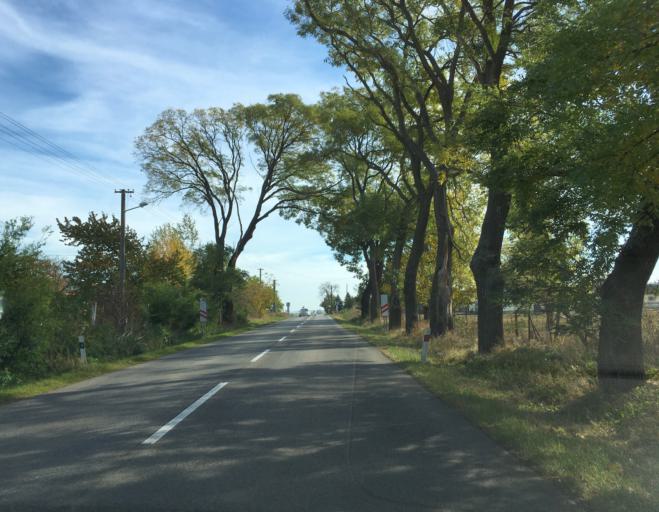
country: SK
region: Nitriansky
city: Zeliezovce
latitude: 48.0974
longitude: 18.5614
